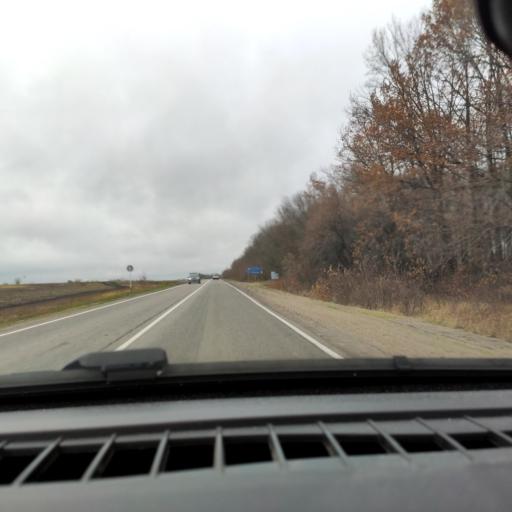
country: RU
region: Voronezj
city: Shilovo
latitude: 51.3837
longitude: 39.0098
